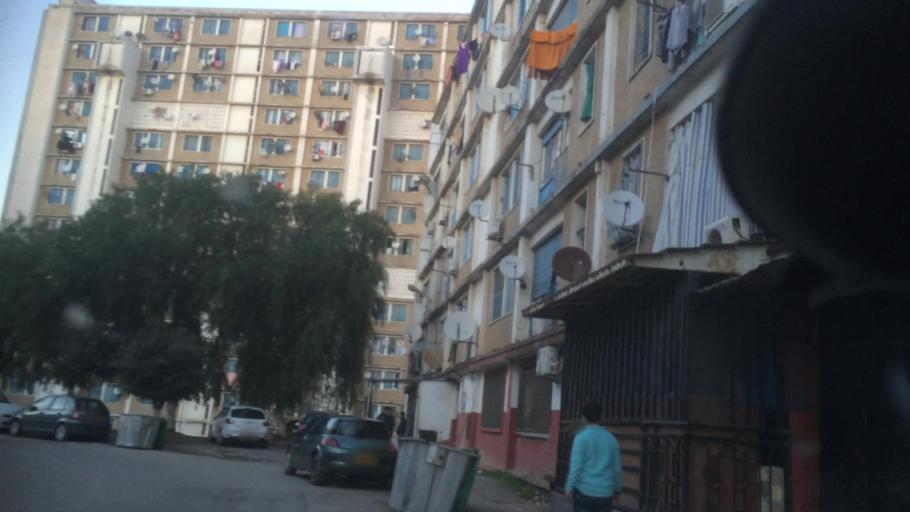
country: DZ
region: Alger
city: Bab Ezzouar
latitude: 36.7262
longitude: 3.1260
